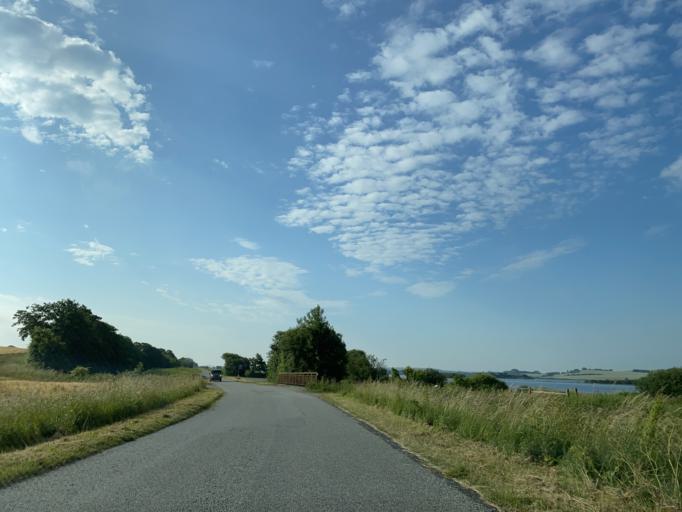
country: DK
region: South Denmark
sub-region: Haderslev Kommune
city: Haderslev
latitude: 55.1743
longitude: 9.4816
